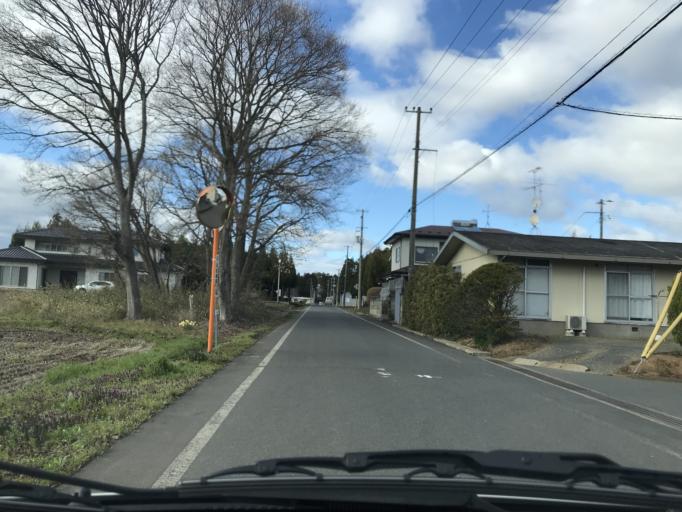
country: JP
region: Iwate
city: Mizusawa
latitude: 39.1139
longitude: 141.0992
